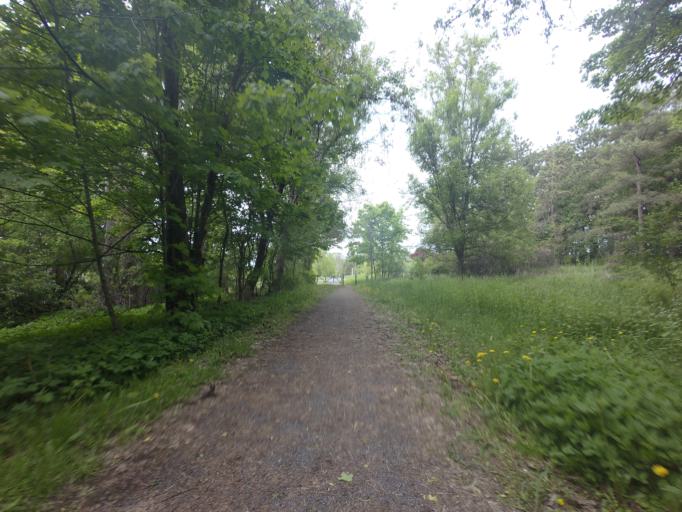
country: CA
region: Ontario
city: Kingston
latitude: 44.3637
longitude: -76.6271
